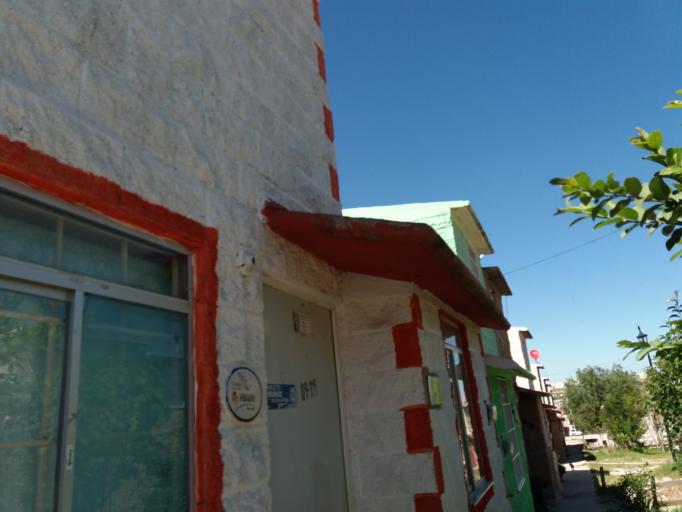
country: MX
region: Aguascalientes
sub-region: Aguascalientes
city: Aguascalientes
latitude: 21.8727
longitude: -102.2353
